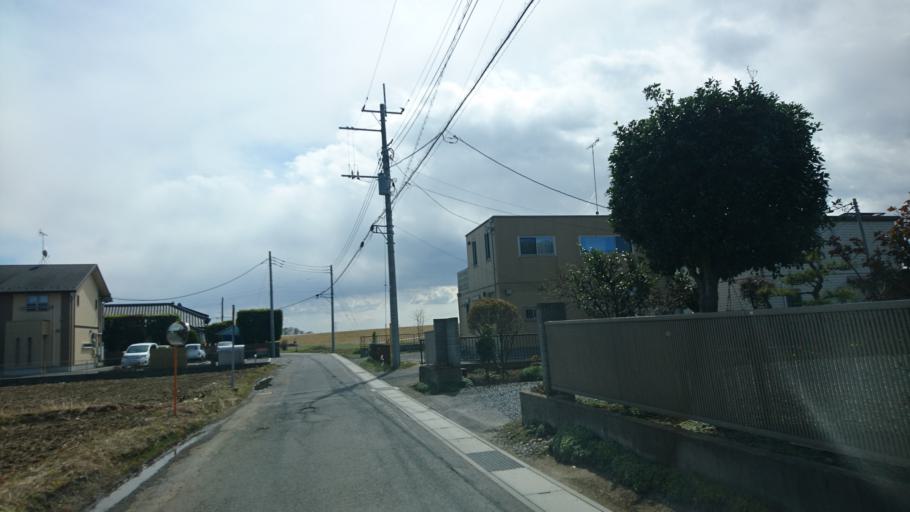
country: JP
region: Ibaraki
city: Yuki
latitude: 36.2742
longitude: 139.9070
